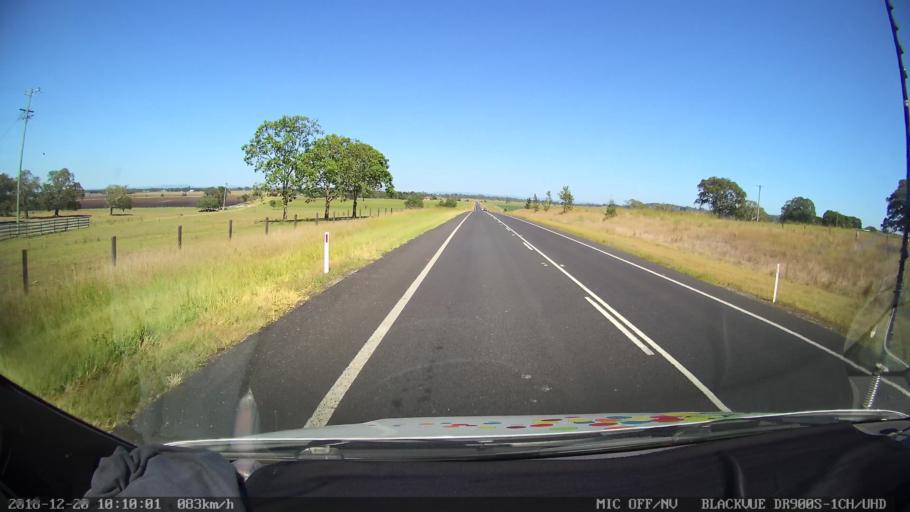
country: AU
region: New South Wales
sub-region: Lismore Municipality
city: Lismore
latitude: -28.8759
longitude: 153.1794
